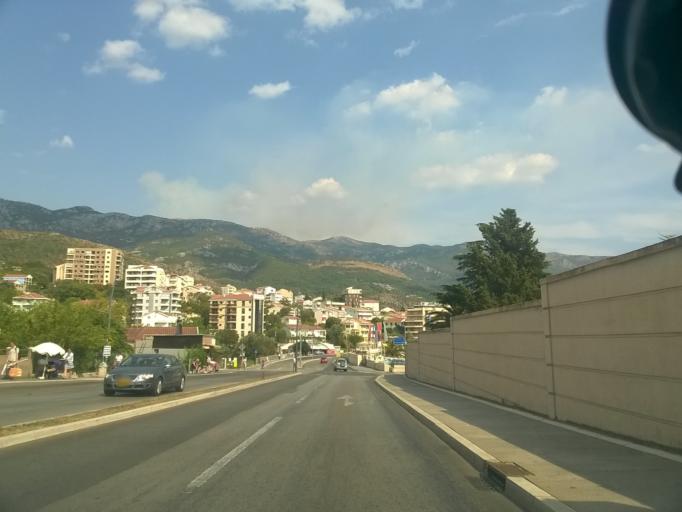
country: ME
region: Budva
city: Budva
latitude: 42.2836
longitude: 18.8622
